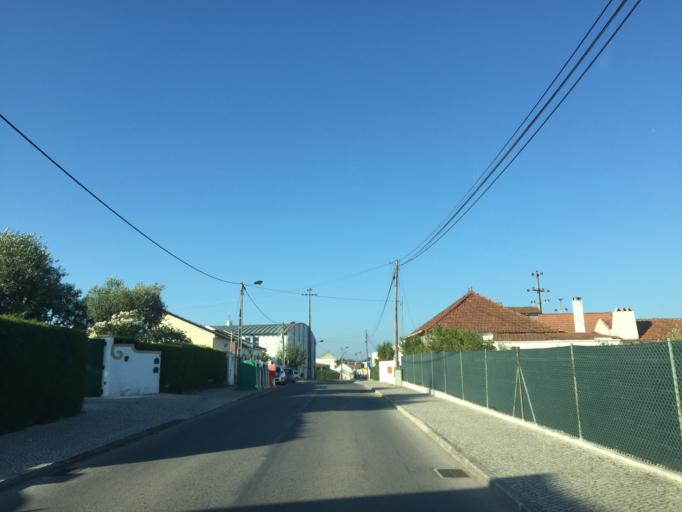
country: PT
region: Lisbon
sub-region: Azambuja
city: Aveiras de Cima
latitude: 39.1345
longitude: -8.9250
